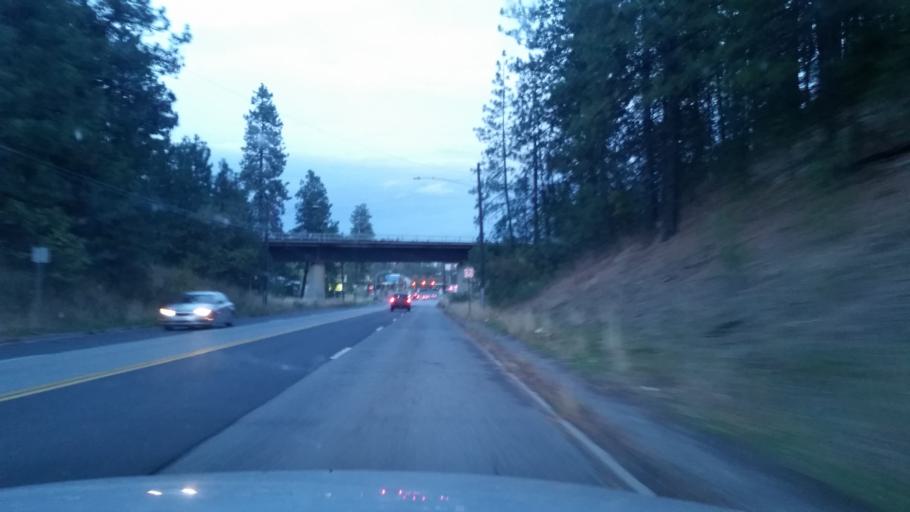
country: US
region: Washington
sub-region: Spokane County
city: Spokane
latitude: 47.6470
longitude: -117.4576
